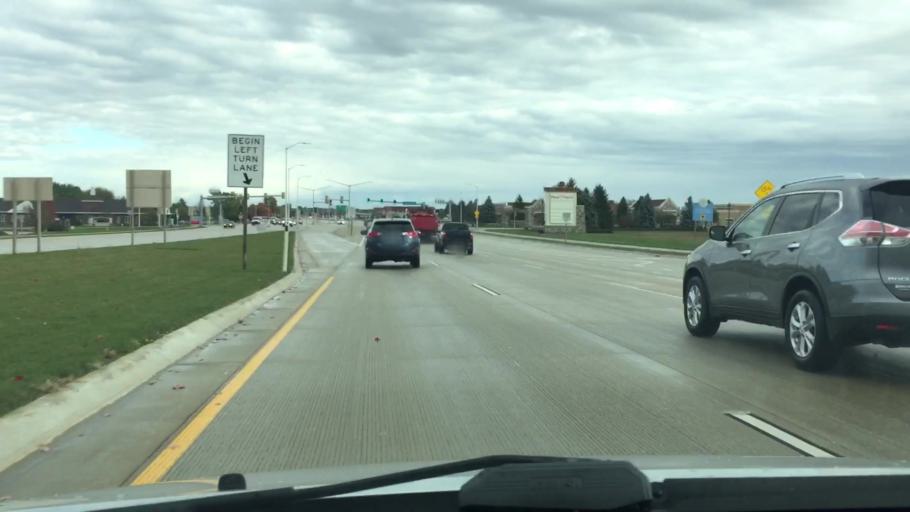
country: US
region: Wisconsin
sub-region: Waukesha County
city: Oconomowoc
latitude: 43.0720
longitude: -88.4709
